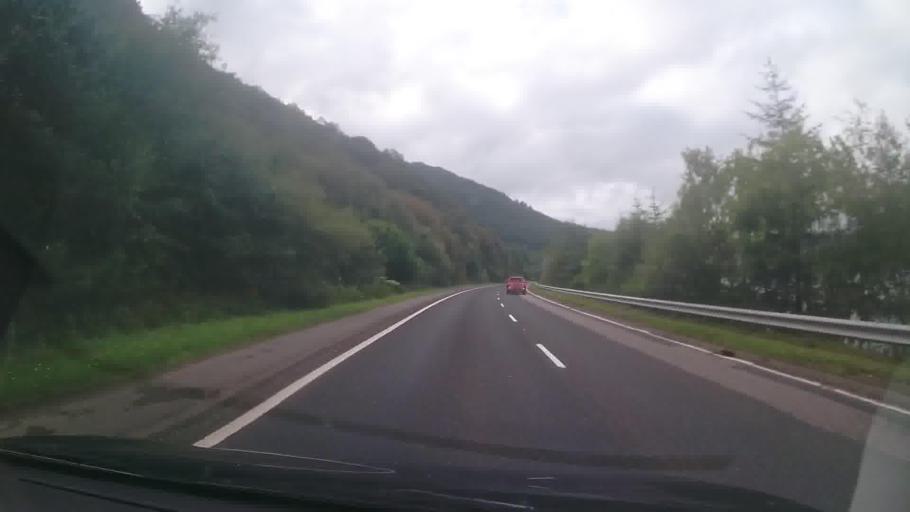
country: GB
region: Scotland
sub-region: Highland
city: Fort William
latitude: 56.6764
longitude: -5.1481
